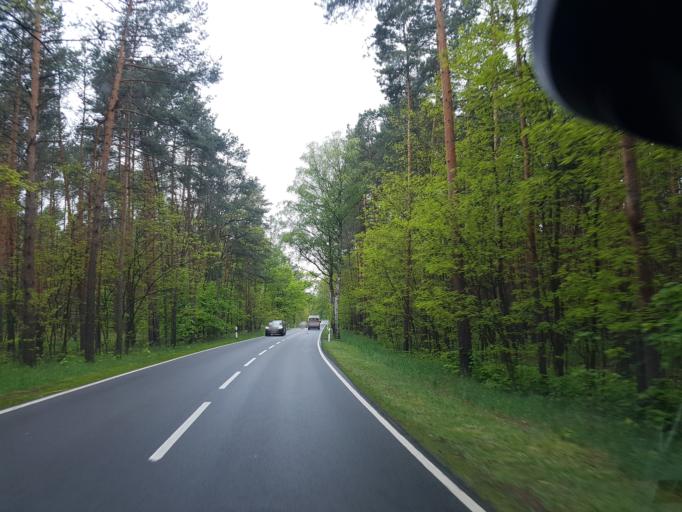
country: DE
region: Saxony
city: Schleife
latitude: 51.6099
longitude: 14.4824
